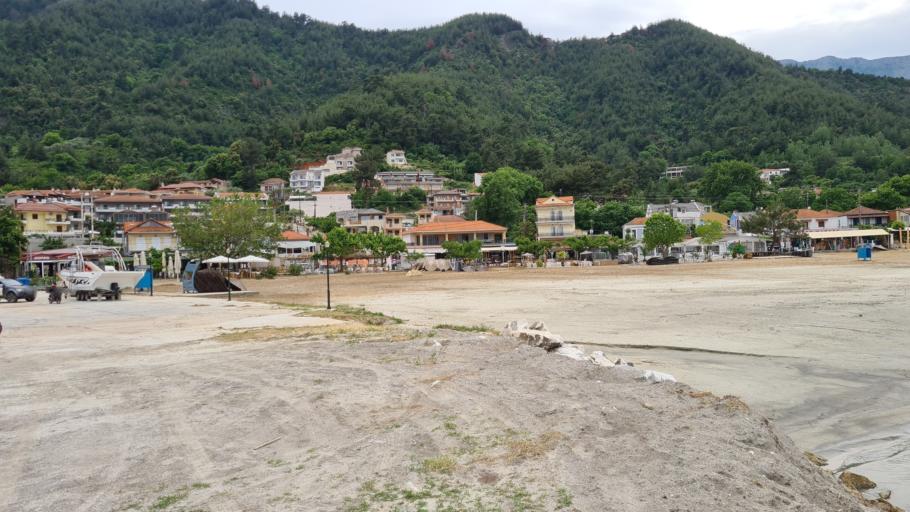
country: GR
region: East Macedonia and Thrace
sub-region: Nomos Kavalas
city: Potamia
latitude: 40.7089
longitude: 24.7619
